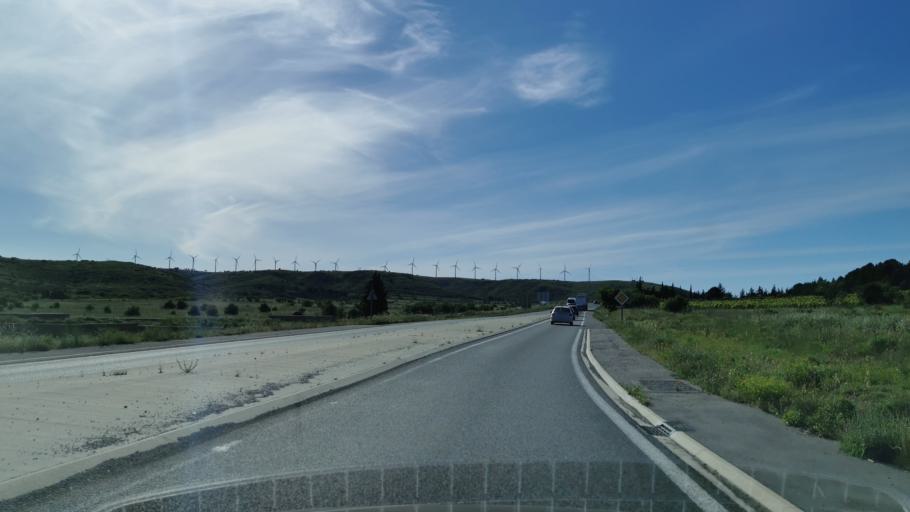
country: FR
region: Languedoc-Roussillon
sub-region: Departement de l'Aude
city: Nevian
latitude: 43.1912
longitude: 2.9086
